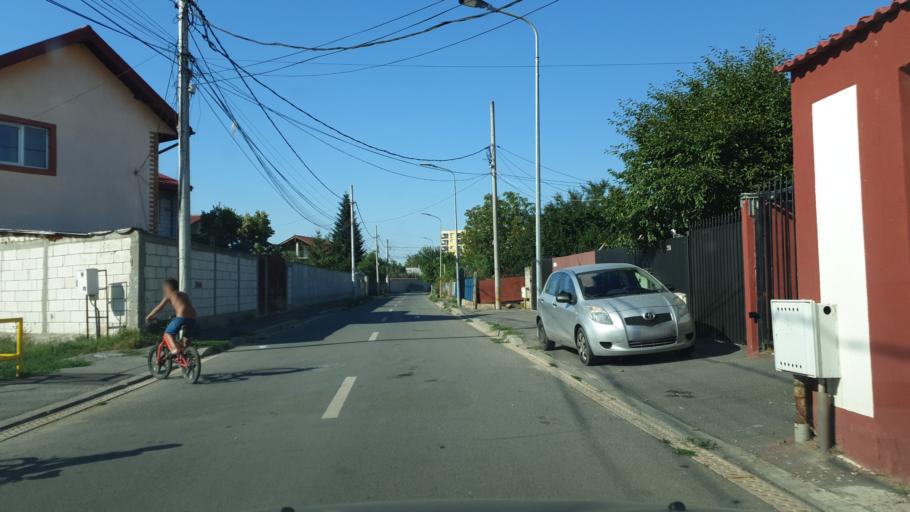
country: RO
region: Ilfov
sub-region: Comuna Chiajna
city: Rosu
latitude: 44.4657
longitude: 26.0213
